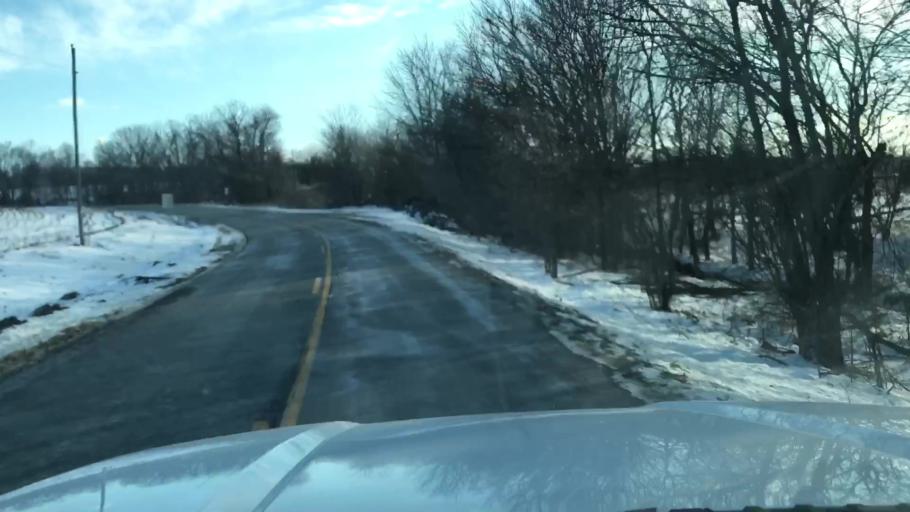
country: US
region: Missouri
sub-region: Holt County
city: Oregon
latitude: 40.1035
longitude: -95.0226
